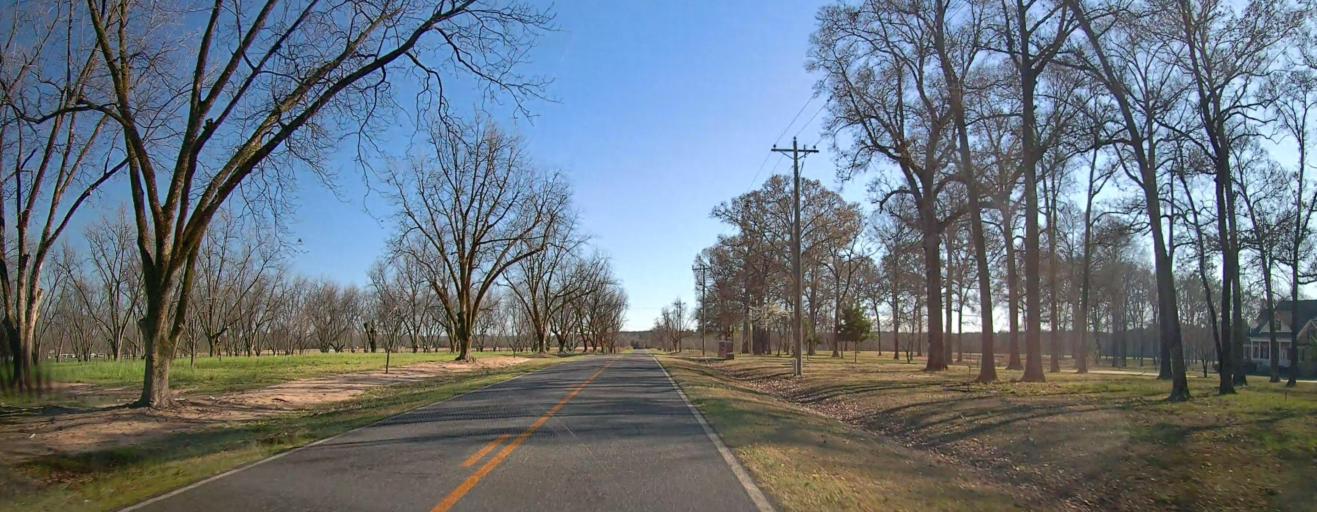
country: US
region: Georgia
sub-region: Peach County
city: Fort Valley
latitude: 32.6022
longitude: -83.8523
